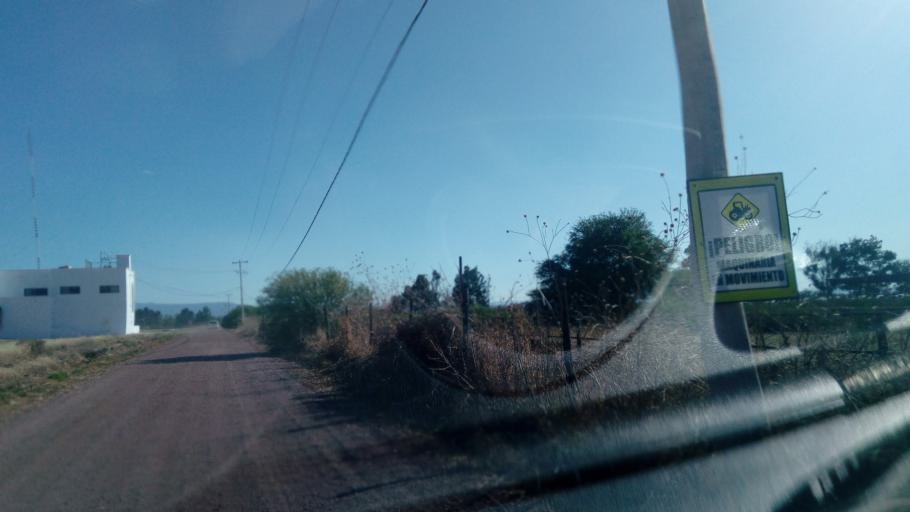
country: MX
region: Durango
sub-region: Durango
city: Jose Refugio Salcido
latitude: 24.0170
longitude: -104.5534
